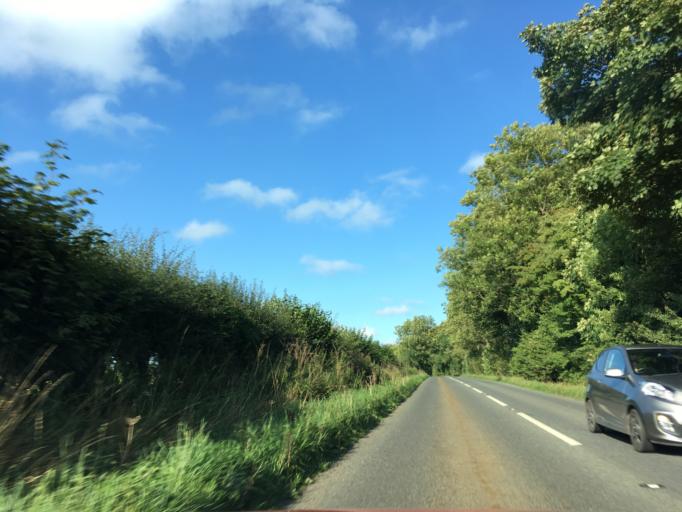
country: GB
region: England
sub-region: Somerset
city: Chilcompton
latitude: 51.2539
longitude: -2.5618
